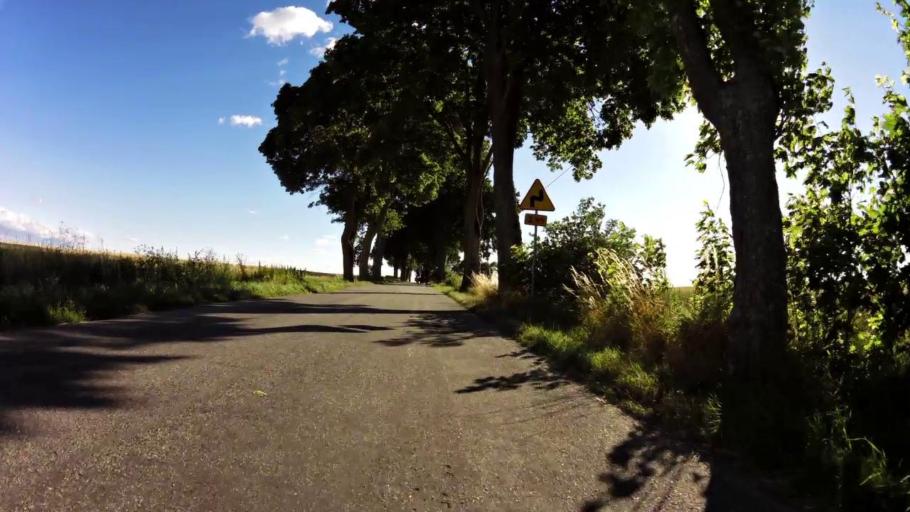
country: PL
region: West Pomeranian Voivodeship
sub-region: Powiat swidwinski
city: Swidwin
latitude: 53.7624
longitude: 15.7049
